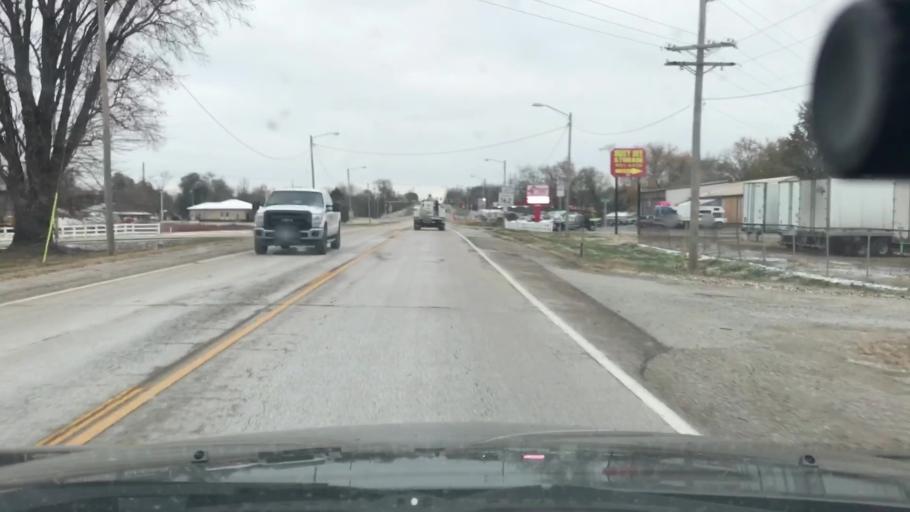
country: US
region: Illinois
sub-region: Madison County
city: Pontoon Beach
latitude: 38.7183
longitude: -90.0707
